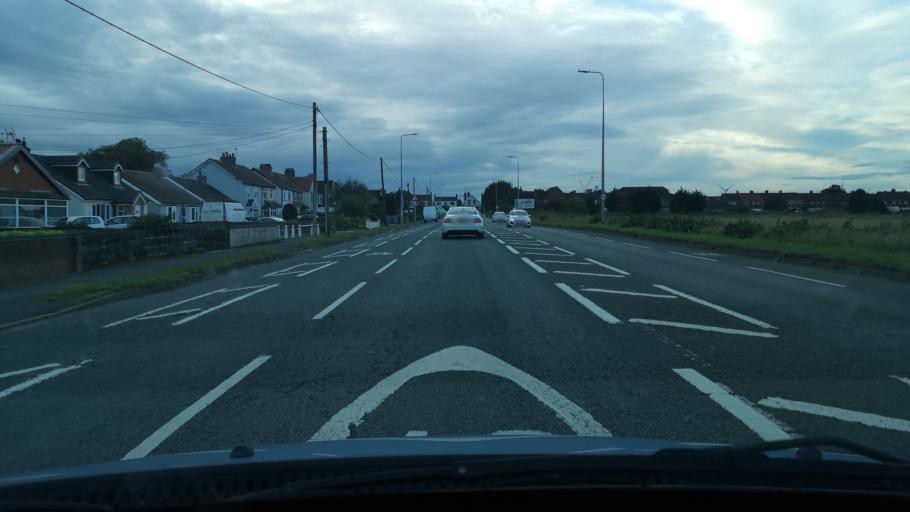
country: GB
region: England
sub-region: North Lincolnshire
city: Gunness
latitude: 53.5903
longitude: -0.7236
